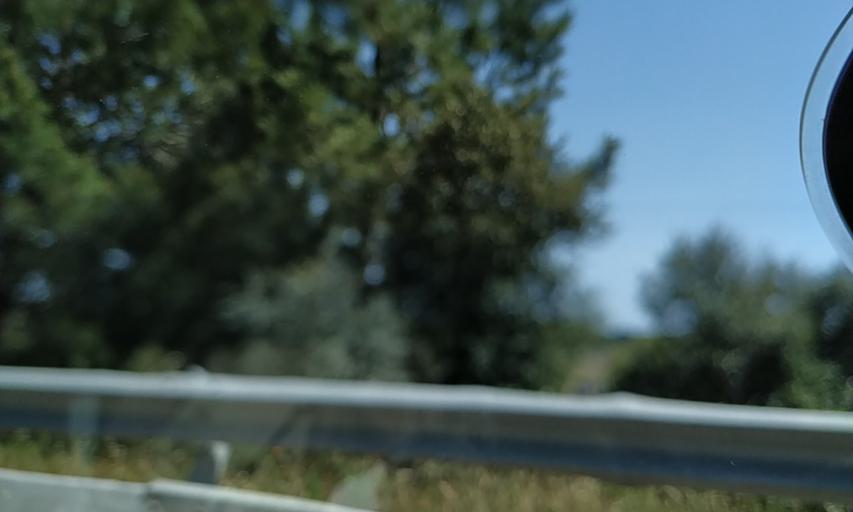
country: PT
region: Setubal
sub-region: Palmela
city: Palmela
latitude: 38.6204
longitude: -8.7470
